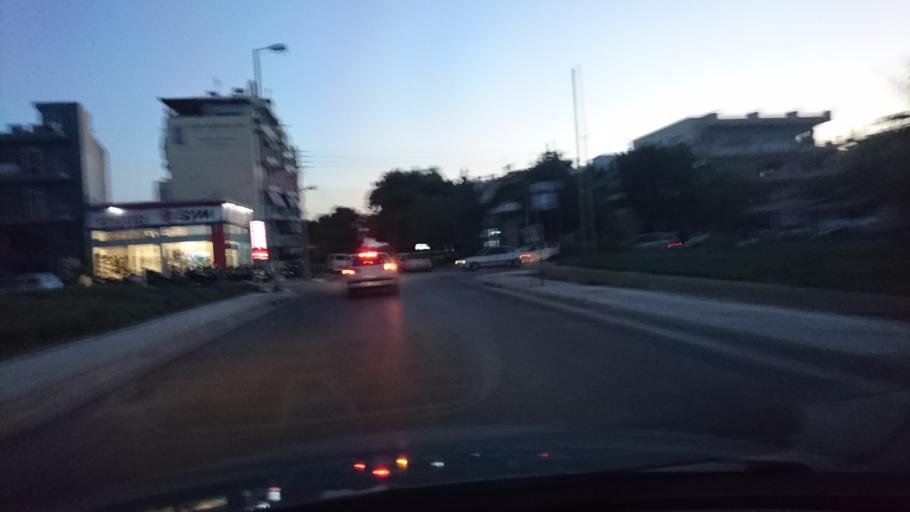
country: GR
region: Attica
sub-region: Nomarchia Athinas
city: Argyroupoli
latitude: 37.9087
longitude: 23.7446
